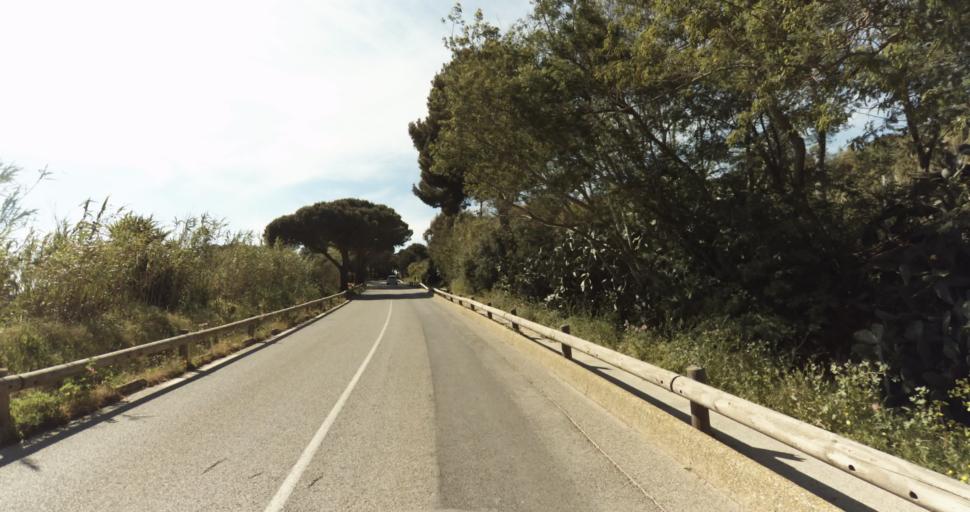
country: FR
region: Provence-Alpes-Cote d'Azur
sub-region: Departement du Var
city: Hyeres
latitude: 43.0314
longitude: 6.1522
